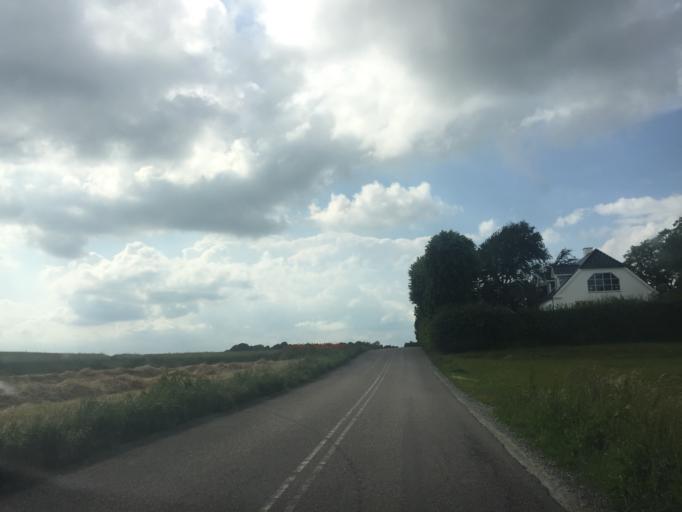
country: DK
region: Capital Region
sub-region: Hoje-Taastrup Kommune
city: Flong
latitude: 55.6883
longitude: 12.1758
